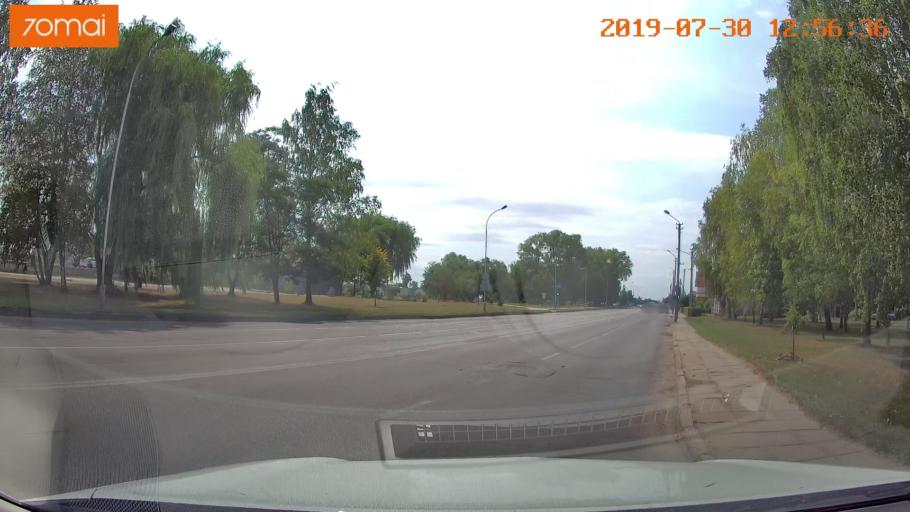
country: LT
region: Marijampoles apskritis
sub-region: Marijampole Municipality
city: Marijampole
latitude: 54.5608
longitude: 23.3653
